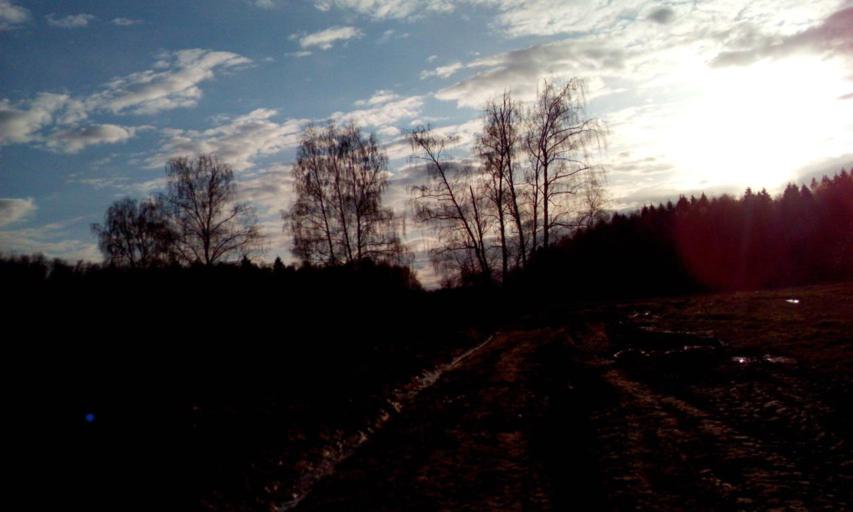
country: RU
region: Moskovskaya
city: Annino
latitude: 55.5498
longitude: 37.2357
